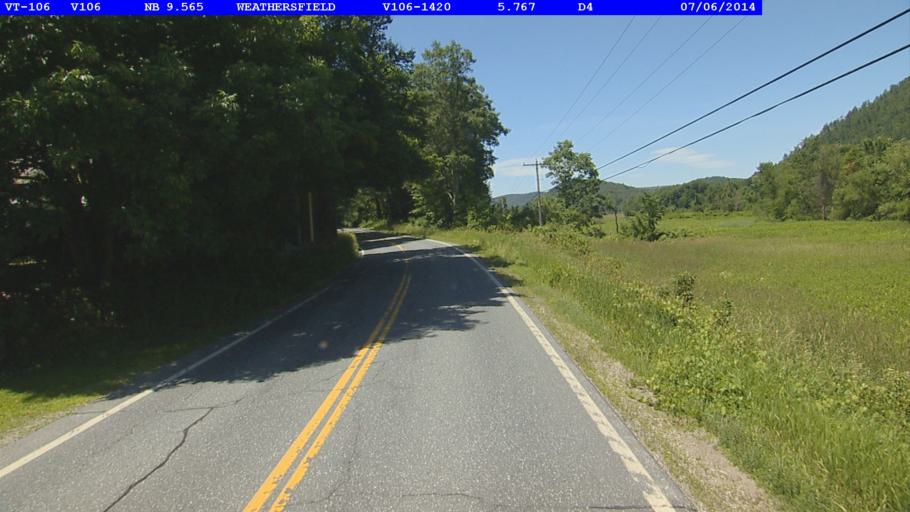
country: US
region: Vermont
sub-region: Windsor County
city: Springfield
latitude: 43.4197
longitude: -72.5196
